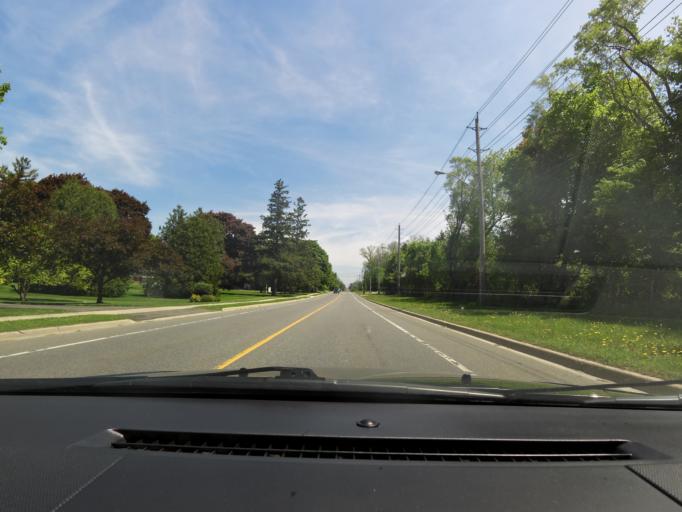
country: CA
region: Ontario
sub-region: Wellington County
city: Guelph
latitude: 43.5274
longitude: -80.2390
